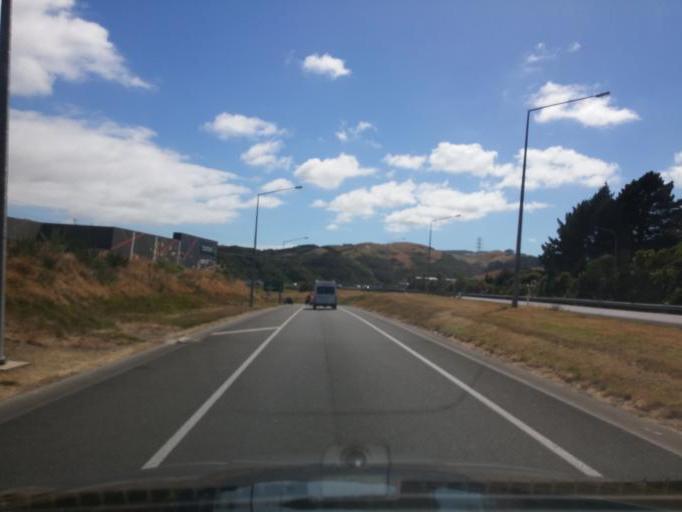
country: NZ
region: Wellington
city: Petone
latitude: -41.1876
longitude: 174.8316
